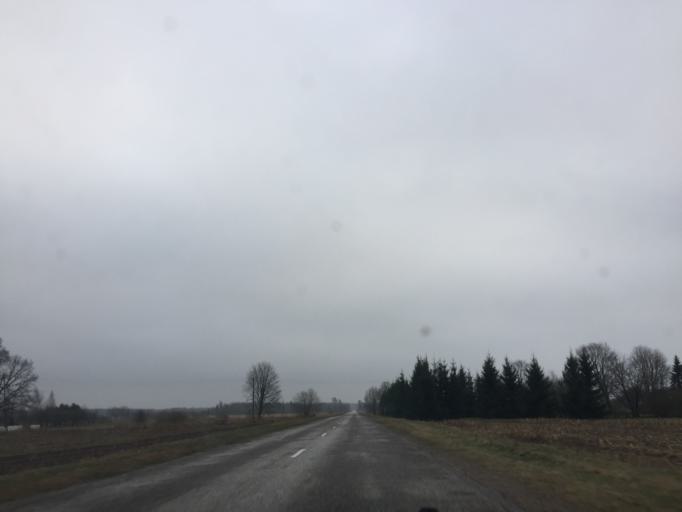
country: LV
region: Limbazu Rajons
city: Limbazi
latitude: 57.5684
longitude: 24.6648
